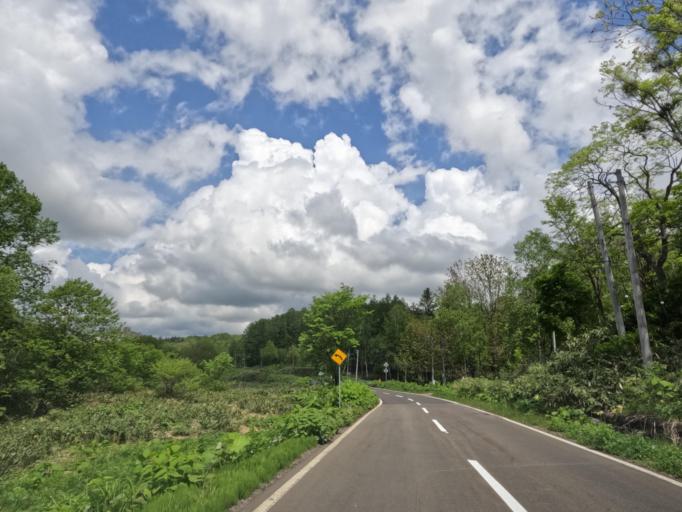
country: JP
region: Hokkaido
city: Takikawa
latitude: 43.5415
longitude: 141.6482
